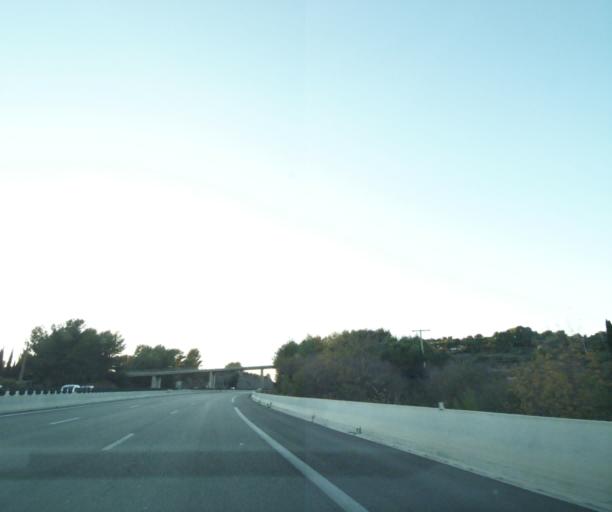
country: FR
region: Provence-Alpes-Cote d'Azur
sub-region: Departement des Bouches-du-Rhone
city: Ceyreste
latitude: 43.1919
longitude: 5.6585
